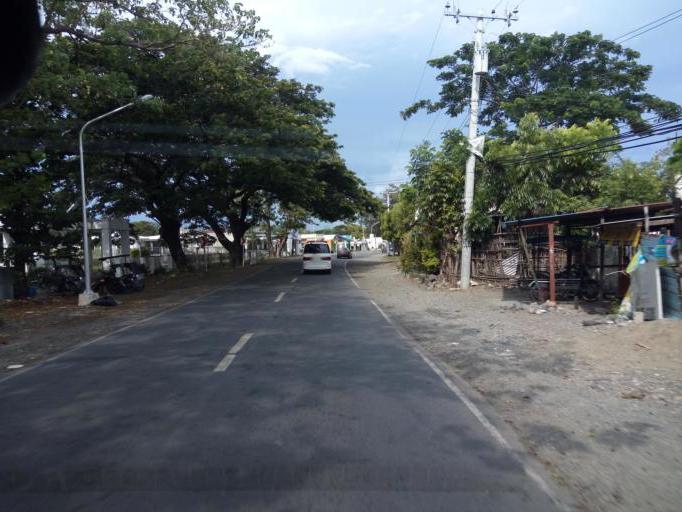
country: PH
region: Central Luzon
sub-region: Province of Nueva Ecija
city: Sibul
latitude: 15.7966
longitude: 120.9822
